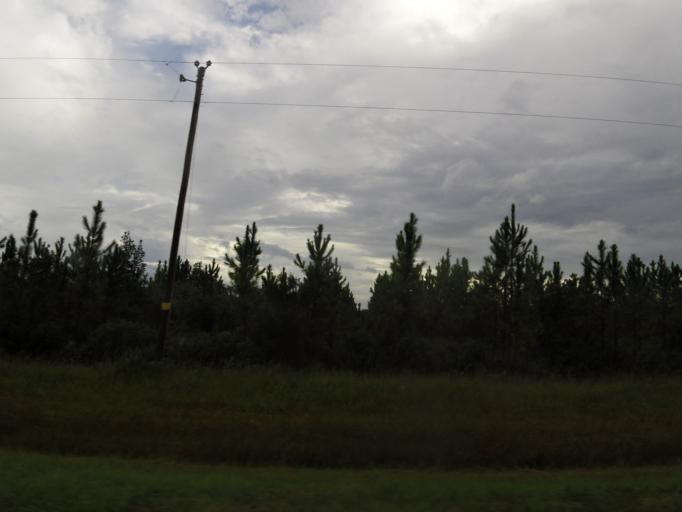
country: US
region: Florida
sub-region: Duval County
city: Baldwin
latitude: 30.3988
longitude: -82.0040
